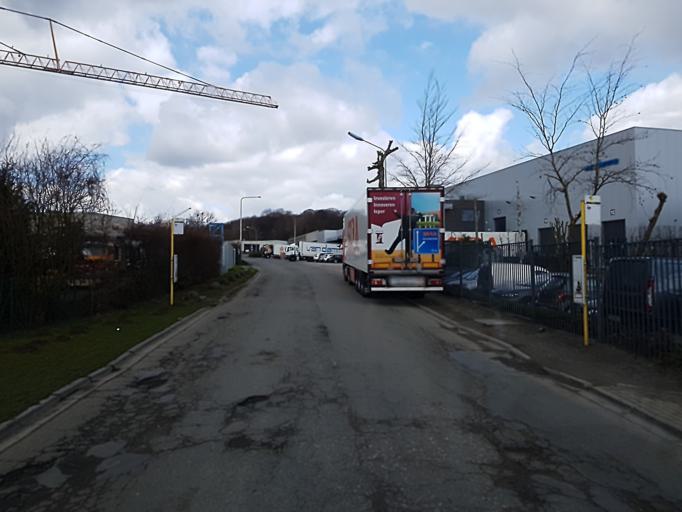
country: BE
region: Flanders
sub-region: Provincie Vlaams-Brabant
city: Ternat
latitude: 50.8878
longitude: 4.1775
